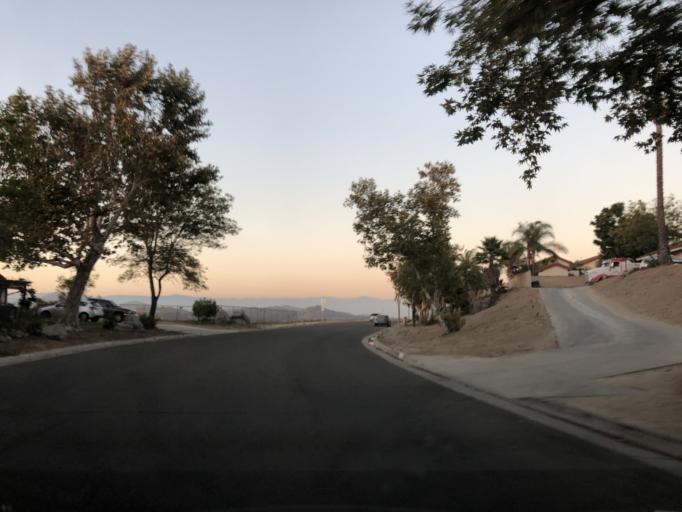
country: US
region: California
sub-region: Riverside County
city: Pedley
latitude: 33.9525
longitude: -117.4949
